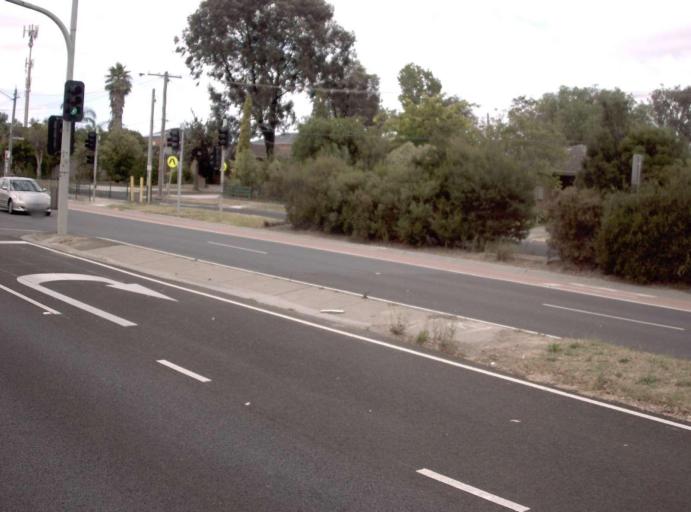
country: AU
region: Victoria
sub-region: Knox
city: Scoresby
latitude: -37.8893
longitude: 145.2329
